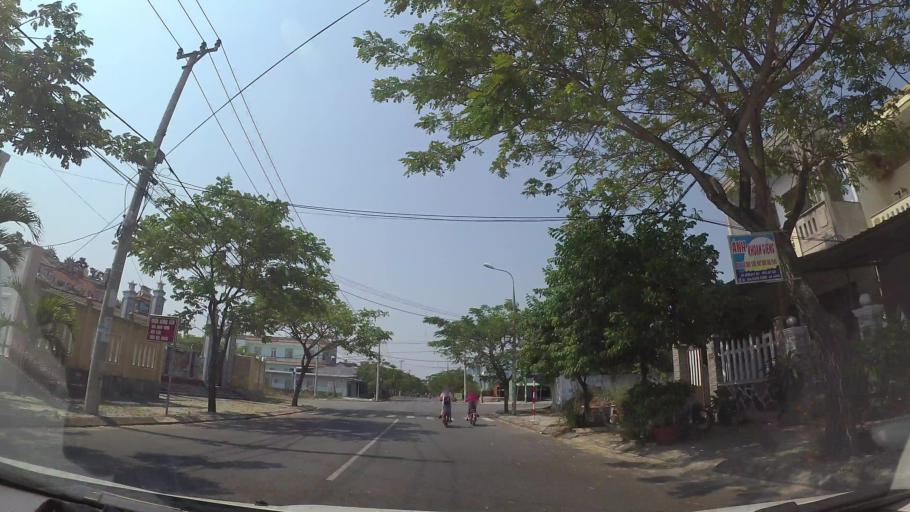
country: VN
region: Da Nang
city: Ngu Hanh Son
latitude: 15.9867
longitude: 108.2696
